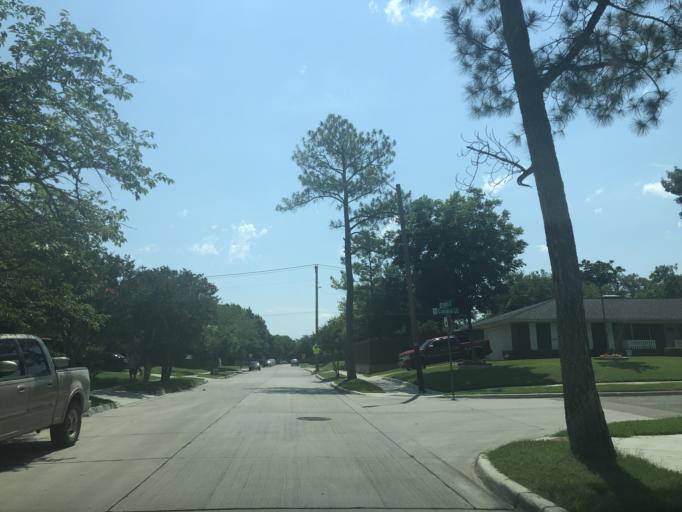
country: US
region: Texas
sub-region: Dallas County
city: Grand Prairie
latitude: 32.7243
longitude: -97.0027
